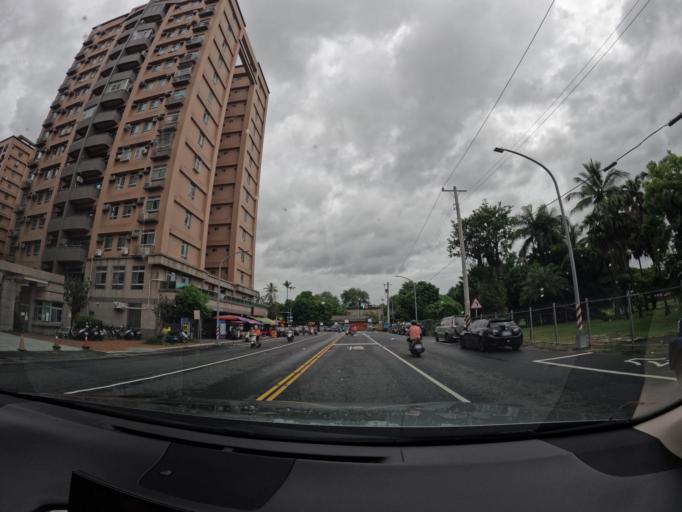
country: TW
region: Taiwan
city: Fengshan
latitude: 22.6290
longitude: 120.3739
